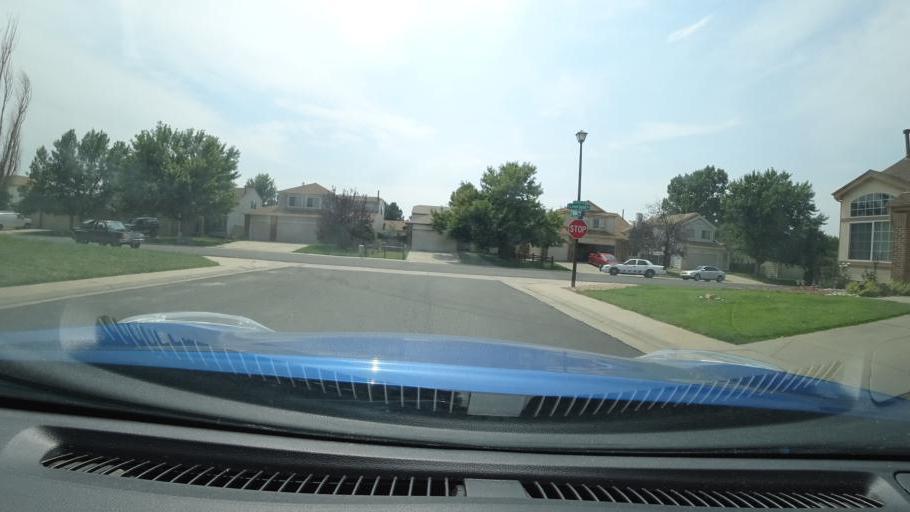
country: US
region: Colorado
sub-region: Adams County
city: Aurora
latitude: 39.7772
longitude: -104.7447
